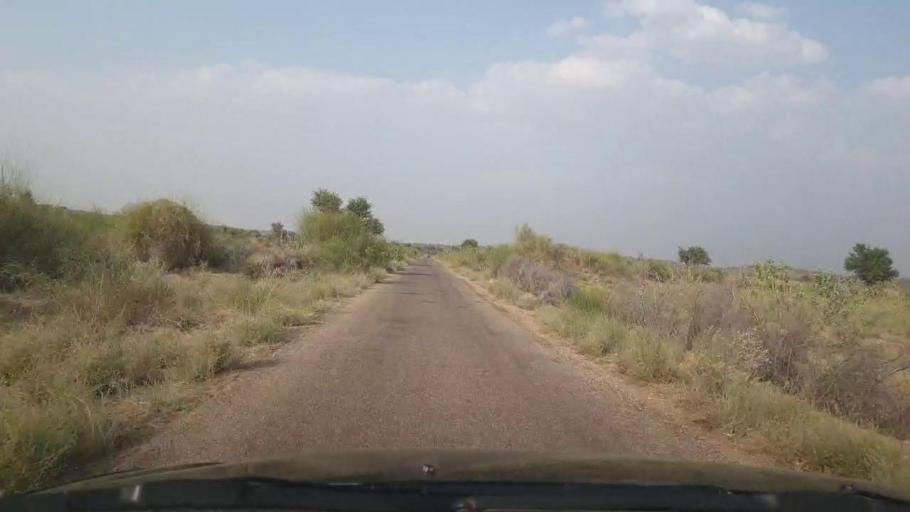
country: PK
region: Sindh
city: Islamkot
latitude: 25.0614
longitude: 70.5619
